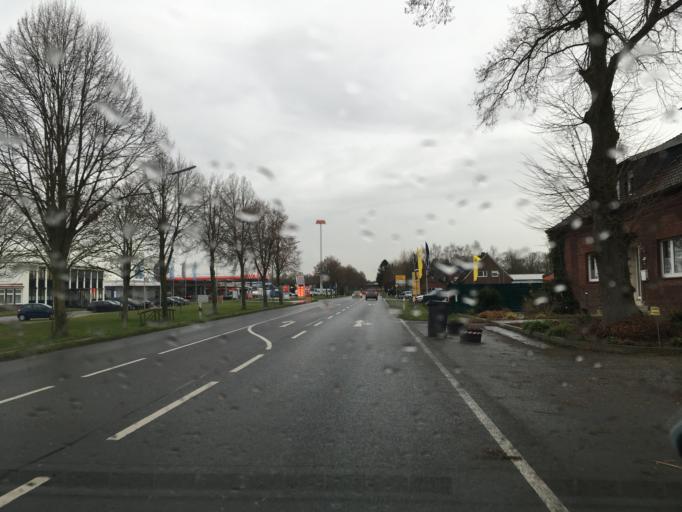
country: DE
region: North Rhine-Westphalia
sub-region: Regierungsbezirk Munster
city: Gescher
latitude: 51.9431
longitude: 7.0237
